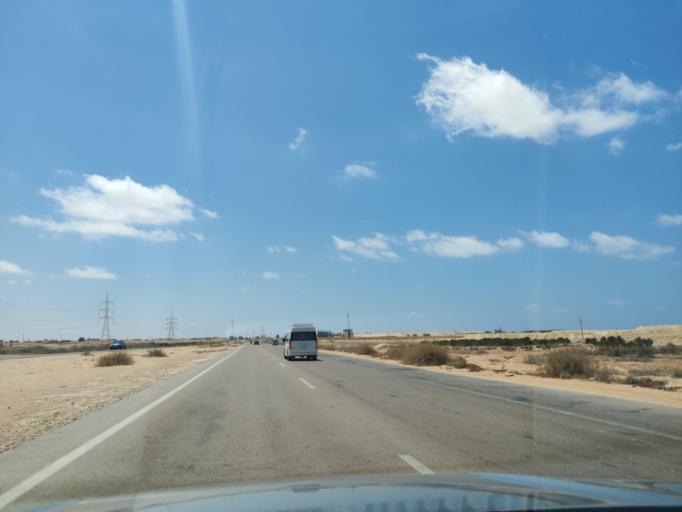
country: EG
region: Muhafazat Matruh
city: Al `Alamayn
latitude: 31.0583
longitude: 28.2126
